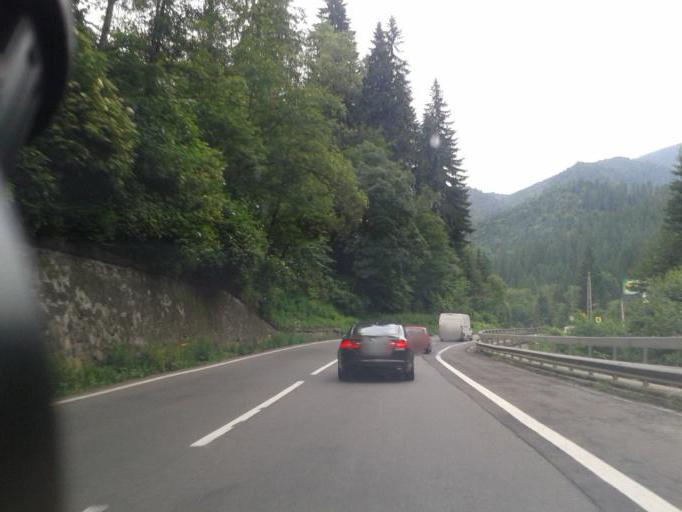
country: RO
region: Brasov
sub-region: Oras Predeal
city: Predeal
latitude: 45.5365
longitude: 25.5860
